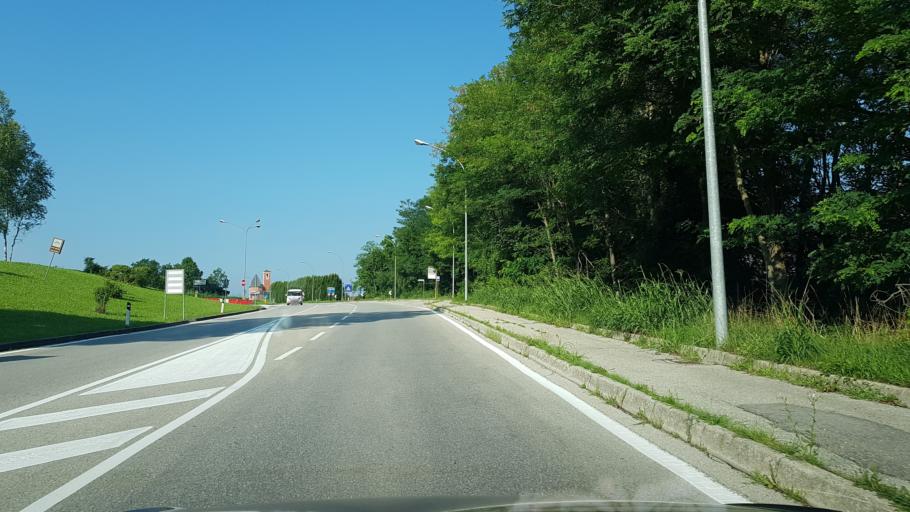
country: IT
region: Veneto
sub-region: Provincia di Belluno
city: Belluno
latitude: 46.1277
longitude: 12.2118
